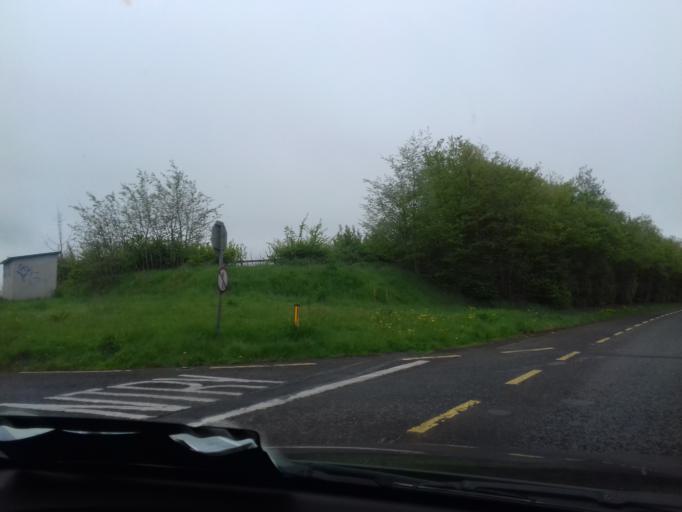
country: IE
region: Leinster
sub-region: Laois
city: Portlaoise
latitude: 53.0469
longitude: -7.2466
